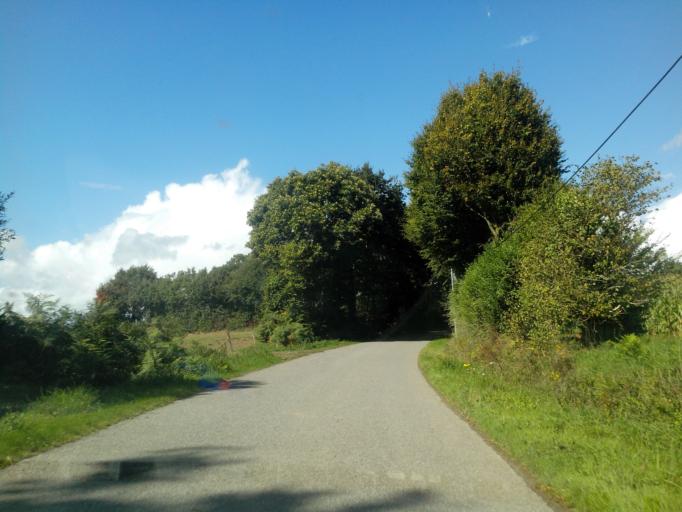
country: FR
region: Brittany
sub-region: Departement des Cotes-d'Armor
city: Merdrignac
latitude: 48.1449
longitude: -2.4117
